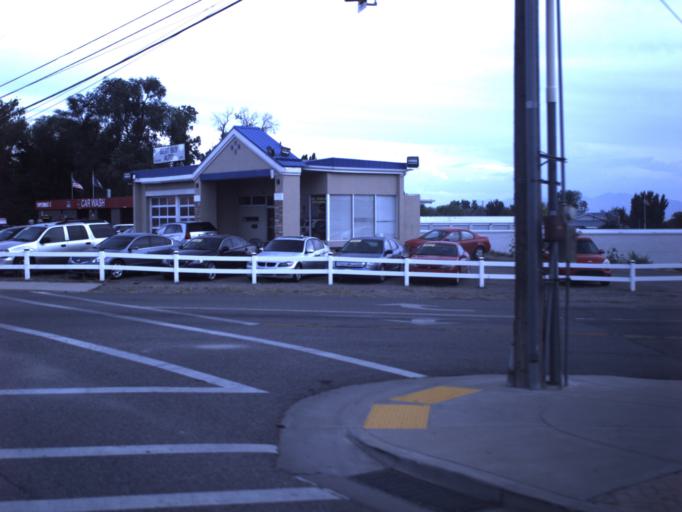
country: US
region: Utah
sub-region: Davis County
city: Clearfield
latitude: 41.1111
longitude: -112.0236
